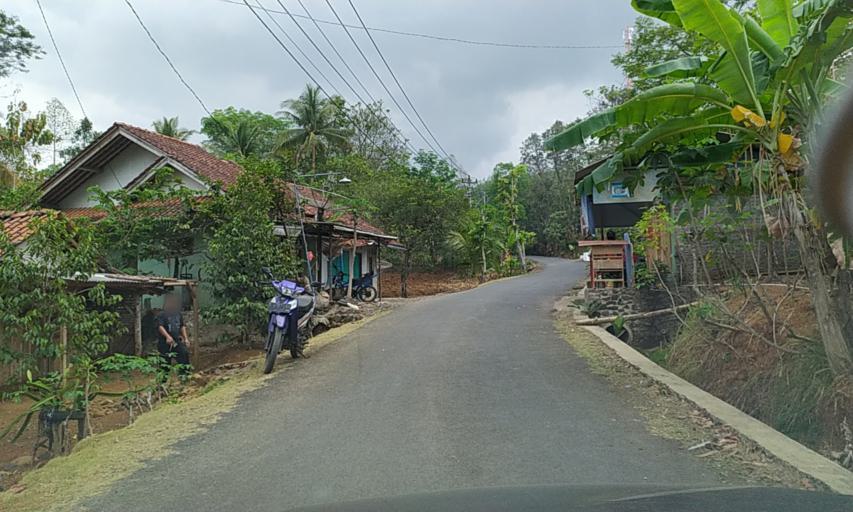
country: ID
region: Central Java
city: Kubang
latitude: -7.2886
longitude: 108.6296
